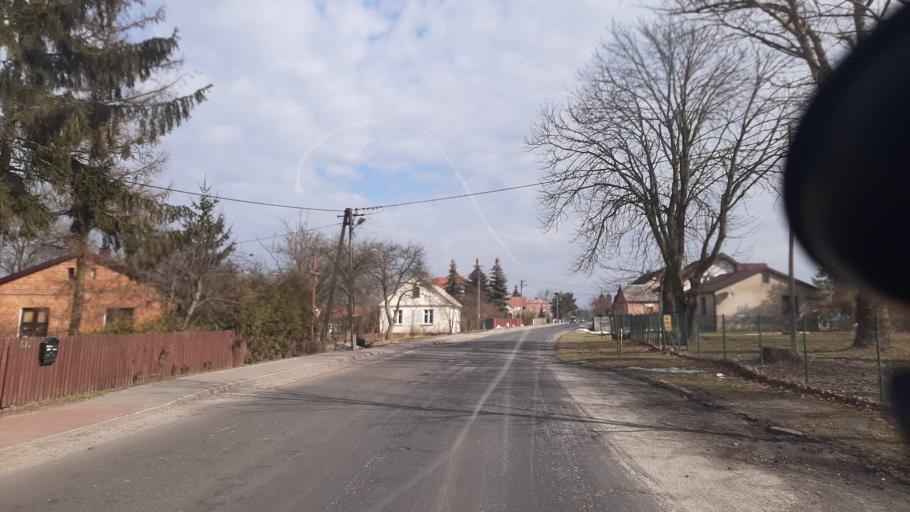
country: PL
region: Lublin Voivodeship
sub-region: Powiat lubartowski
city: Wola Sernicka
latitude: 51.4667
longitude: 22.7285
